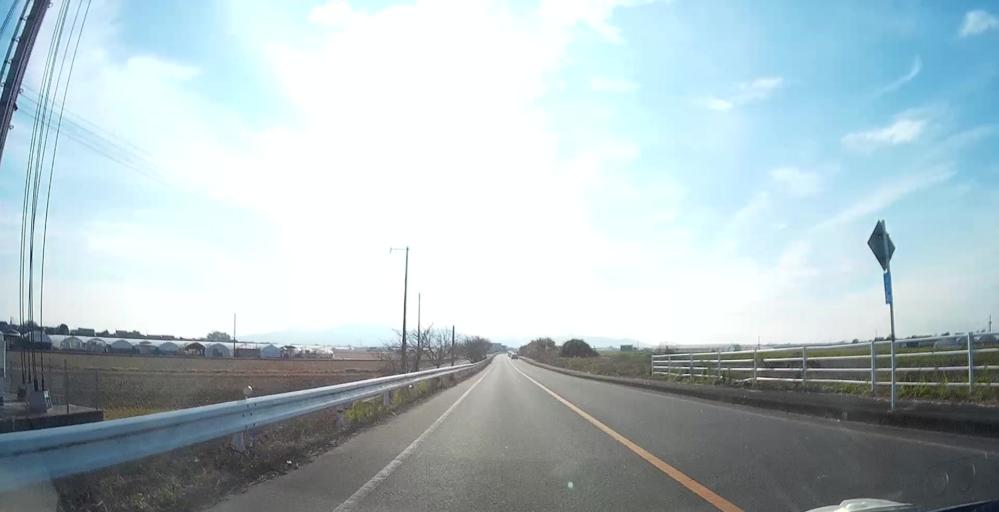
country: JP
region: Kumamoto
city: Uto
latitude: 32.7433
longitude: 130.6732
